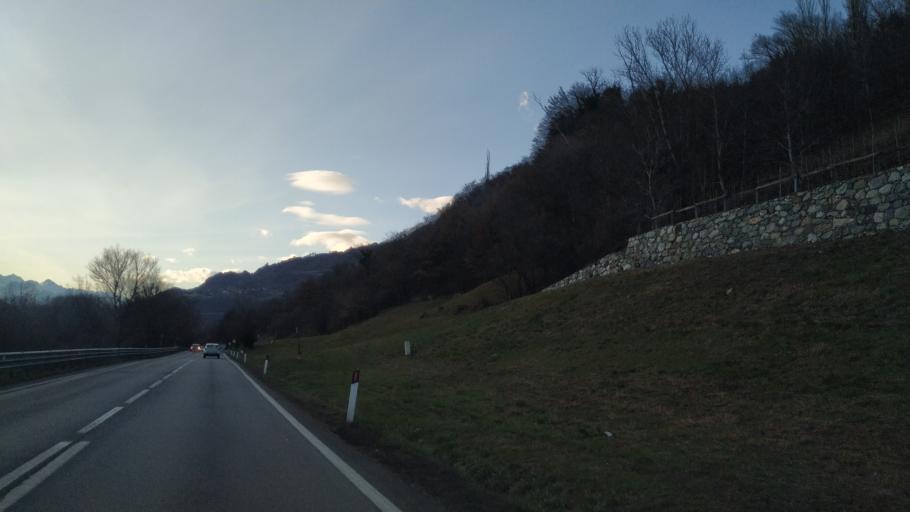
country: IT
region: Aosta Valley
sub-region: Valle d'Aosta
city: Chez Croiset
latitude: 45.7457
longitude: 7.5053
